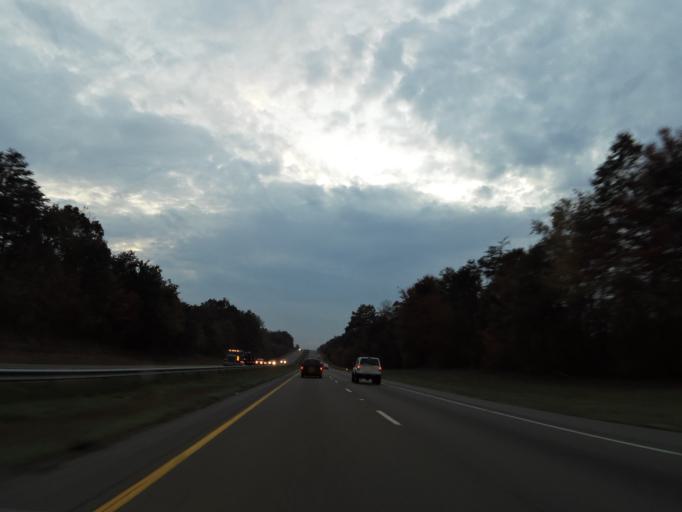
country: US
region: North Carolina
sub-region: Burke County
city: Glen Alpine
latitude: 35.6987
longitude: -81.7998
